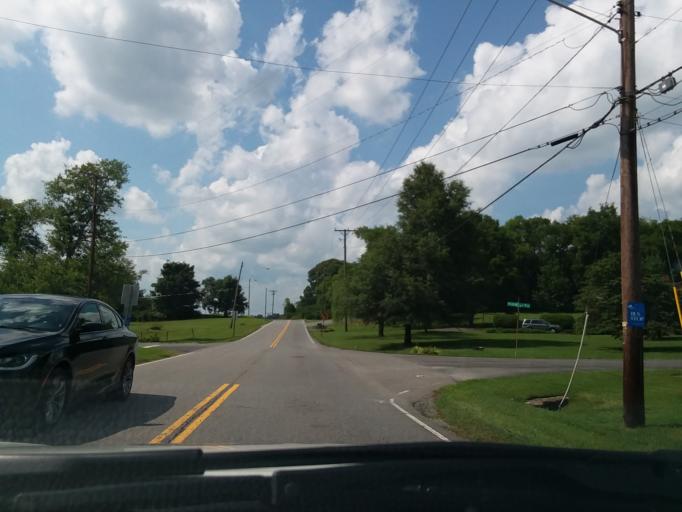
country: US
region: Tennessee
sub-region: Davidson County
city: Lakewood
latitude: 36.2133
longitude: -86.6876
